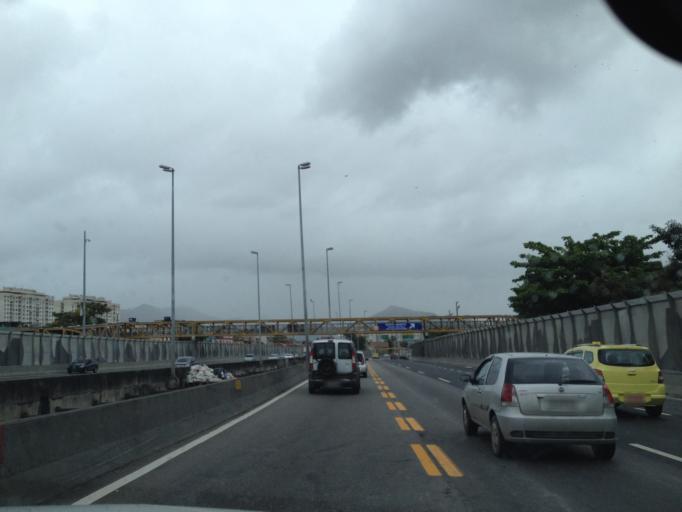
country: BR
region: Rio de Janeiro
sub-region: Rio De Janeiro
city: Rio de Janeiro
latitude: -22.8799
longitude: -43.2792
